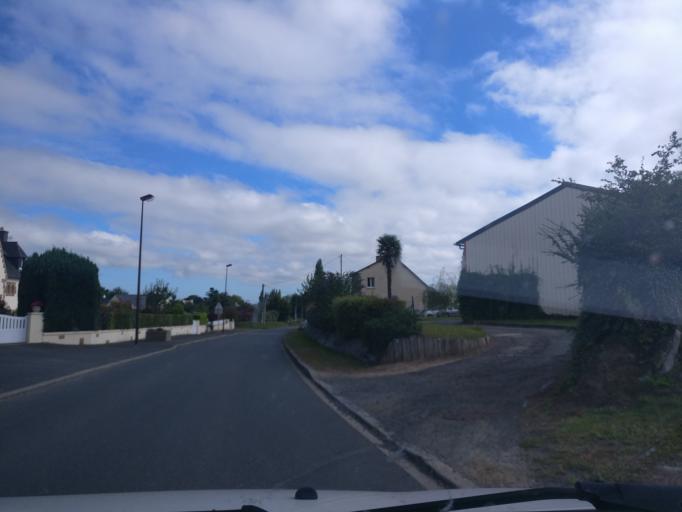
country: FR
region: Brittany
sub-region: Departement des Cotes-d'Armor
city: Rospez
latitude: 48.7319
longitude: -3.3811
